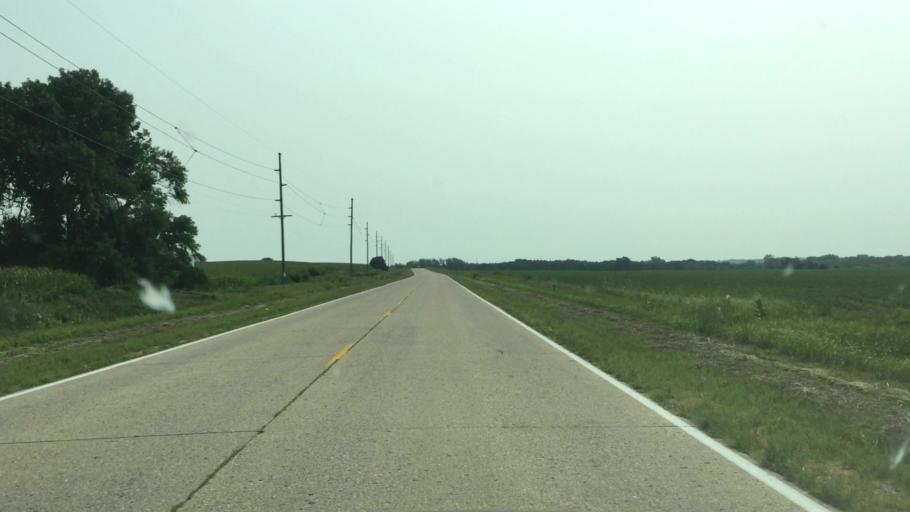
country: US
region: Iowa
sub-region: Dickinson County
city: Milford
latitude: 43.3714
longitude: -95.1927
